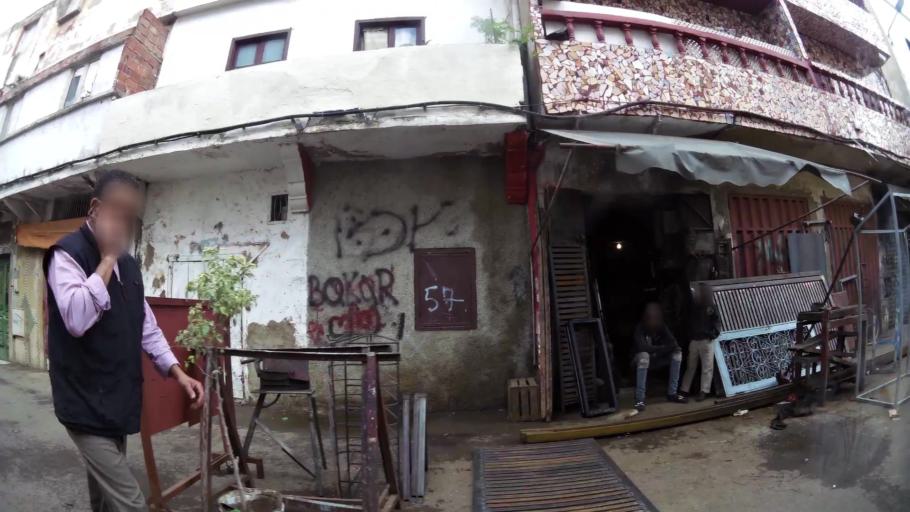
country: MA
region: Grand Casablanca
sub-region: Casablanca
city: Casablanca
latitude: 33.5758
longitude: -7.6306
